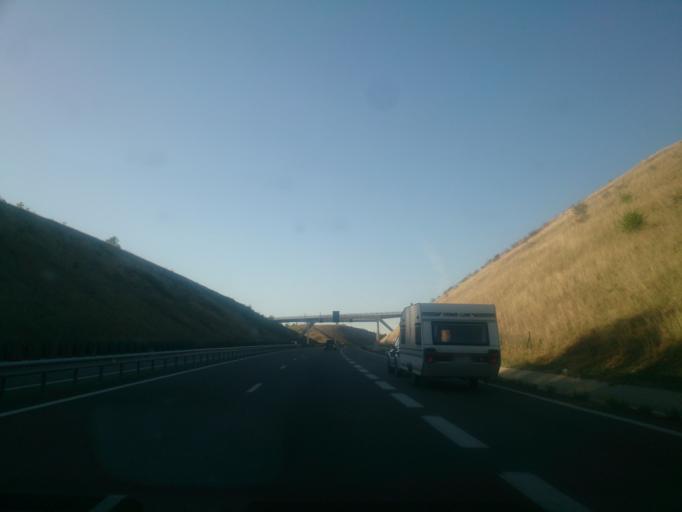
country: FR
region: Midi-Pyrenees
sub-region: Departement du Lot
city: Cahors
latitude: 44.4888
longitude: 1.4962
